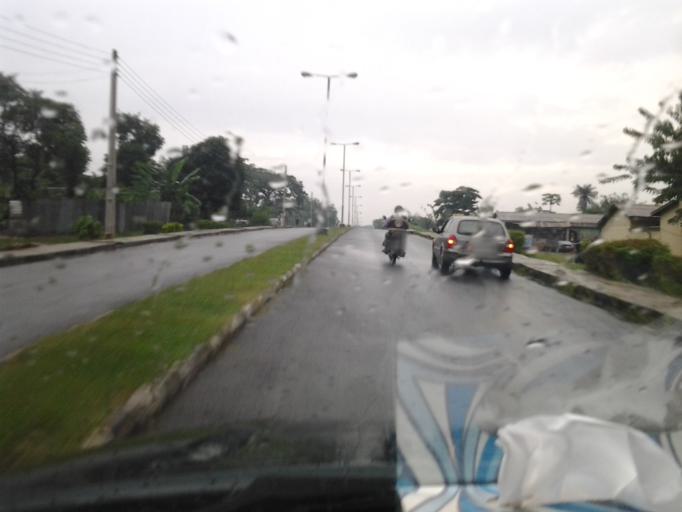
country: NG
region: Oyo
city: Moniya
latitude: 7.4543
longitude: 3.8990
